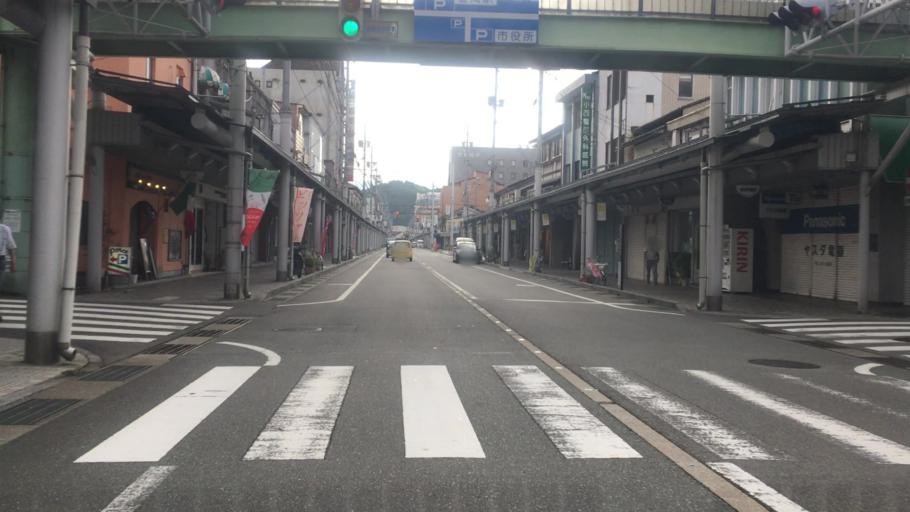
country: JP
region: Hyogo
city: Toyooka
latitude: 35.5438
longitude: 134.8216
